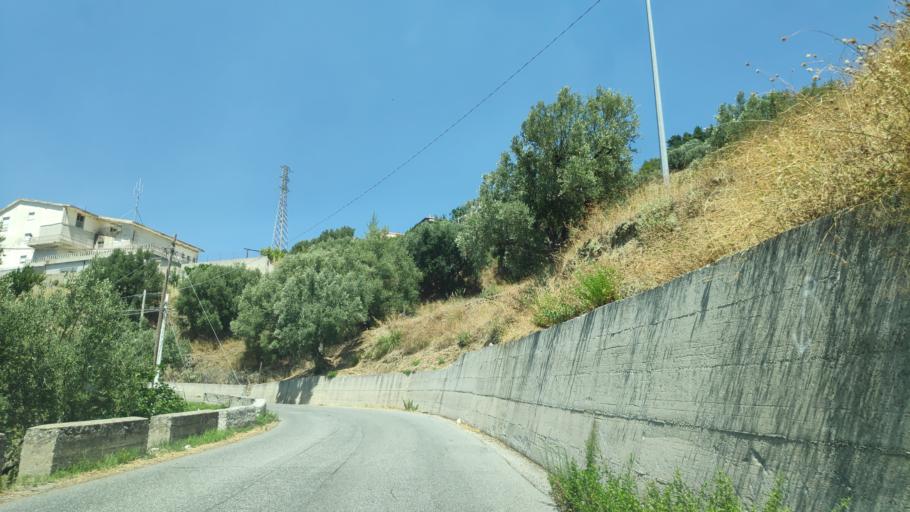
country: IT
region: Calabria
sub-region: Provincia di Reggio Calabria
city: Bova
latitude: 37.9914
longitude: 15.9309
